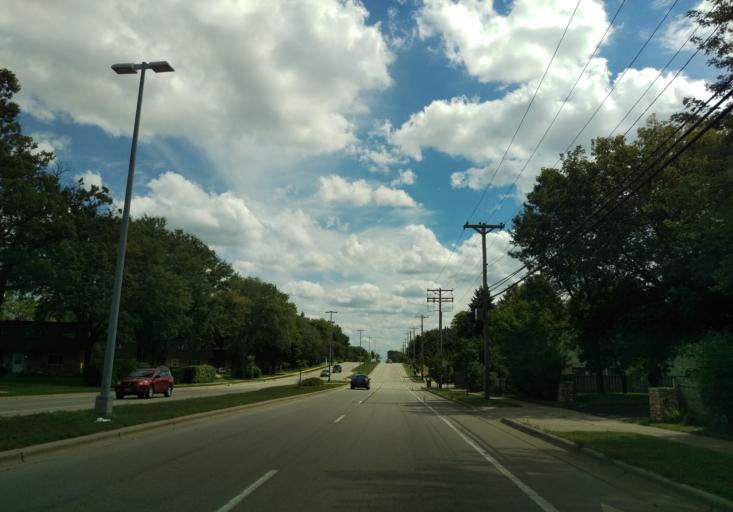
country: US
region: Wisconsin
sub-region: Dane County
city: Maple Bluff
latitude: 43.1397
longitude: -89.3878
